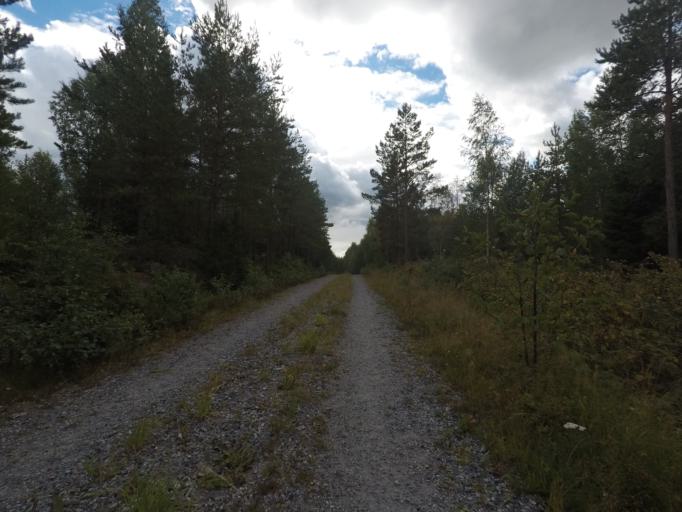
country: SE
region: Soedermanland
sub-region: Eskilstuna Kommun
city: Kvicksund
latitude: 59.4017
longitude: 16.2894
